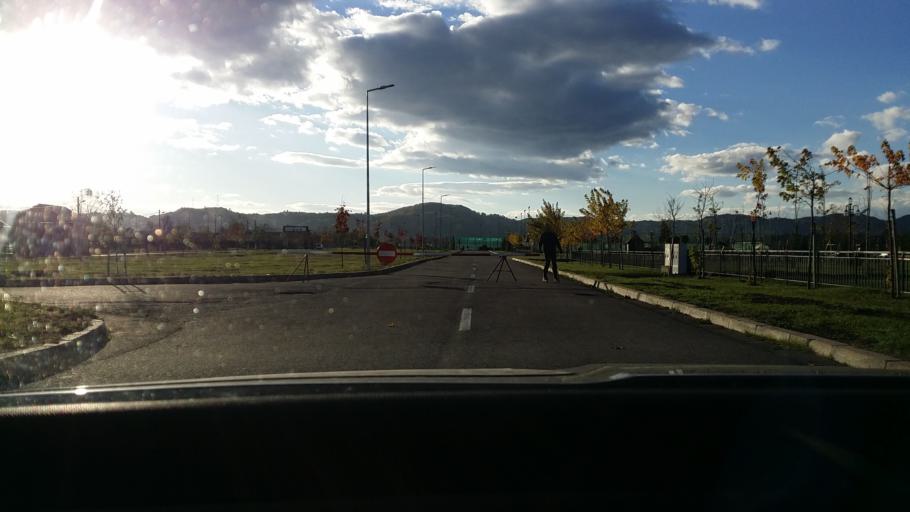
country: RO
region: Prahova
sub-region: Municipiul Campina
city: Campina
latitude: 45.1446
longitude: 25.7299
